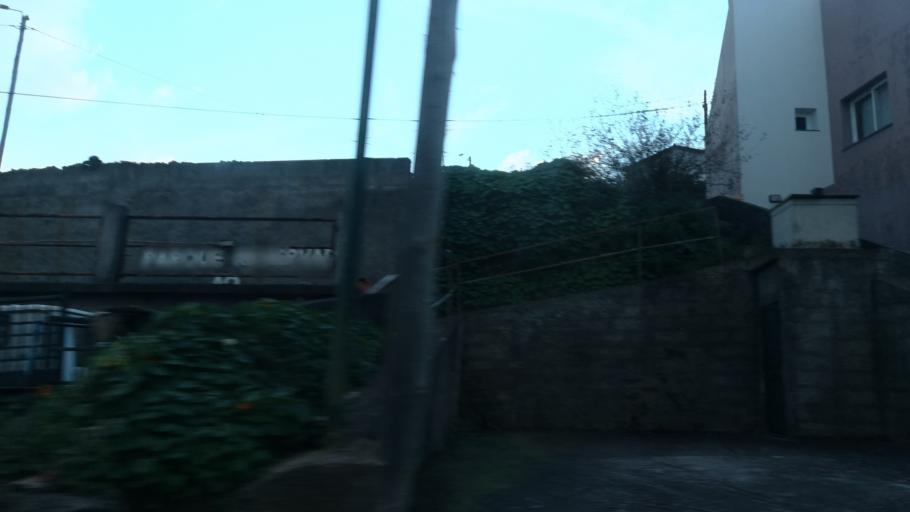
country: PT
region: Madeira
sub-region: Santa Cruz
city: Santa Cruz
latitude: 32.6711
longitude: -16.8184
